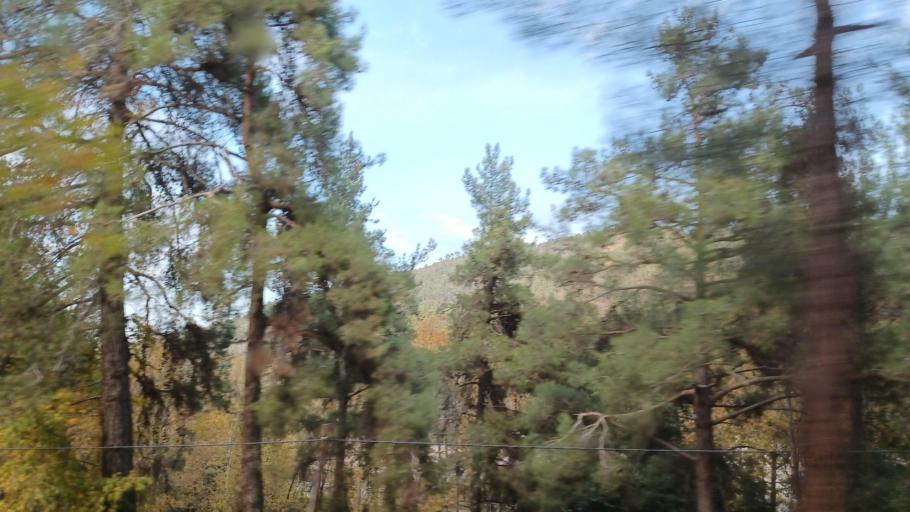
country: CY
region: Lefkosia
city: Kakopetria
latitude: 34.9685
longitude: 32.9187
